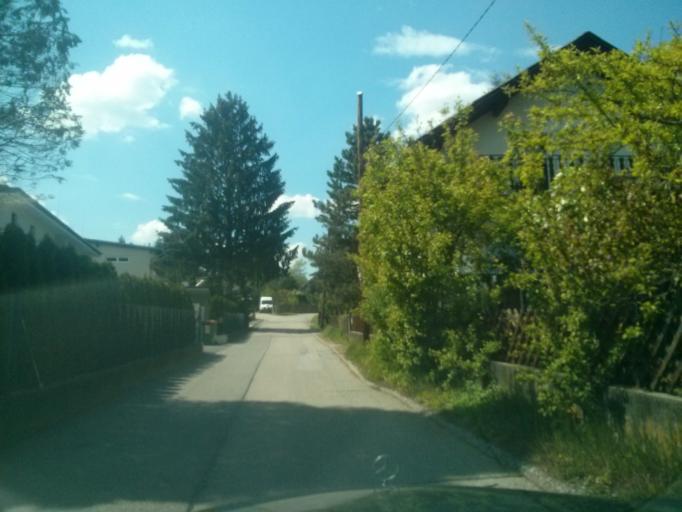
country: AT
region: Styria
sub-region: Politischer Bezirk Graz-Umgebung
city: Stattegg
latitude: 47.1194
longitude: 15.4217
